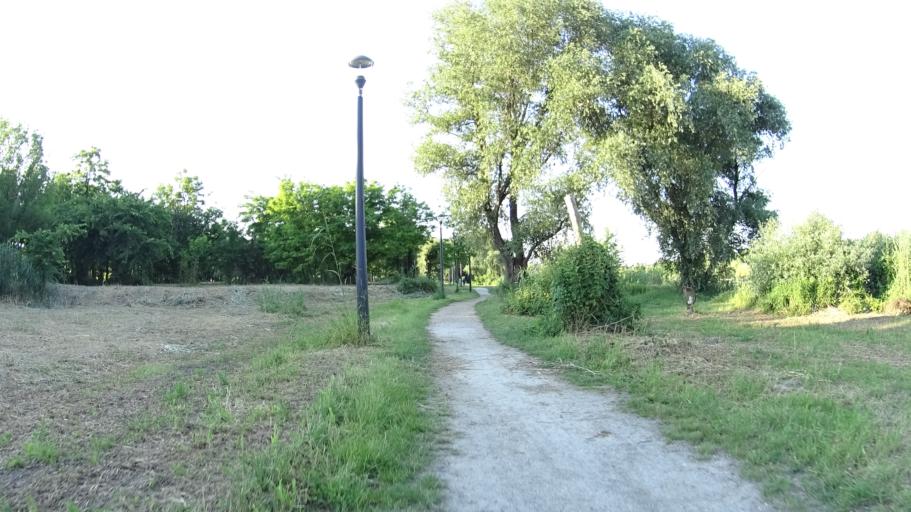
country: HU
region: Budapest
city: Budapest XXIII. keruelet
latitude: 47.3896
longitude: 19.1064
